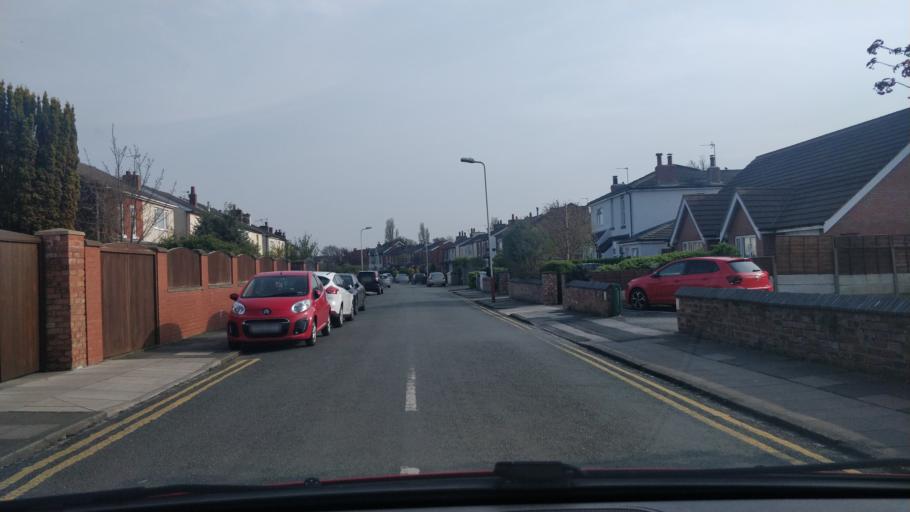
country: GB
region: England
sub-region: Sefton
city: Formby
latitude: 53.6021
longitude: -3.0372
